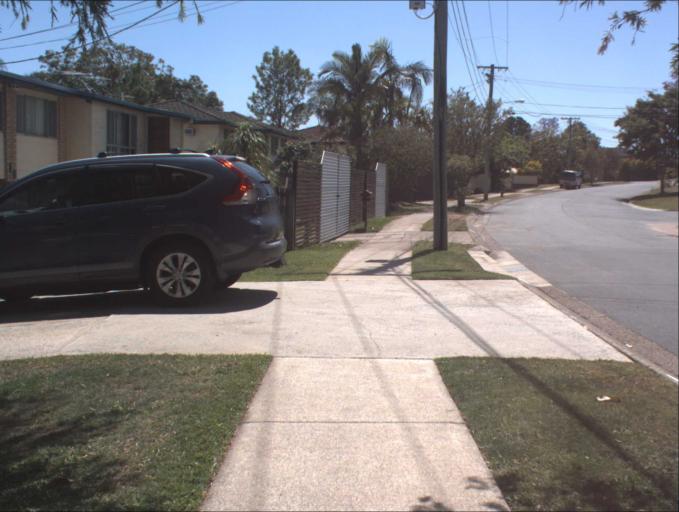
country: AU
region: Queensland
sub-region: Logan
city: Springwood
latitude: -27.6029
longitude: 153.1413
